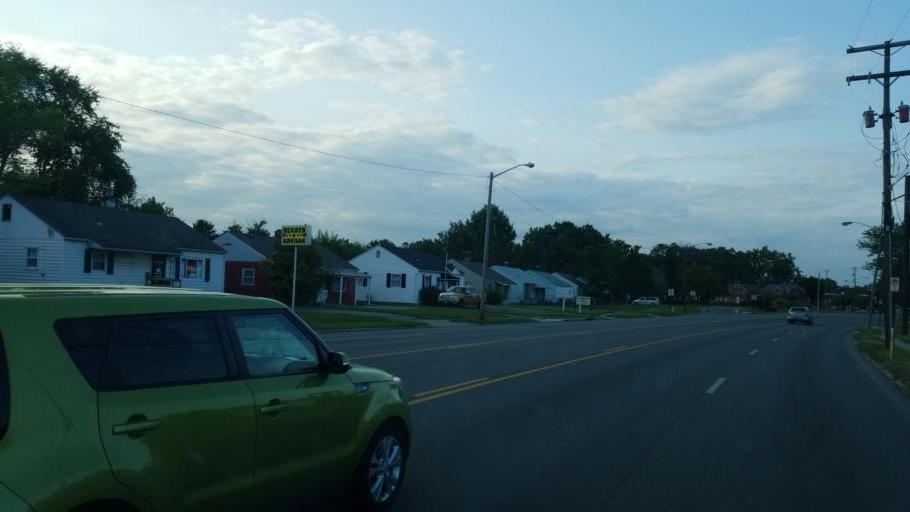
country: US
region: Ohio
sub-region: Franklin County
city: Whitehall
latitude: 39.9714
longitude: -82.8753
